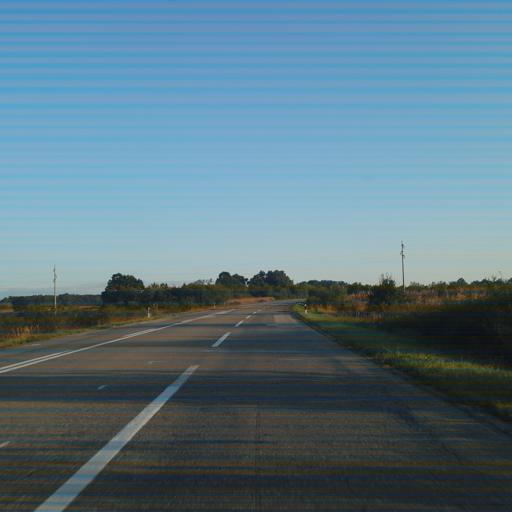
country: RS
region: Central Serbia
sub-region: Borski Okrug
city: Negotin
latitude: 44.1183
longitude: 22.3406
